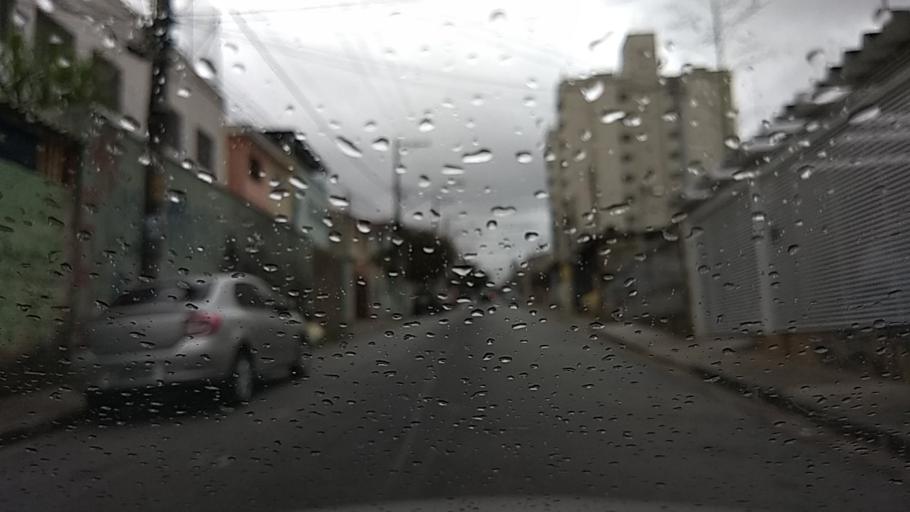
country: BR
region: Sao Paulo
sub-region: Sao Paulo
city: Sao Paulo
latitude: -23.5014
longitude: -46.5964
